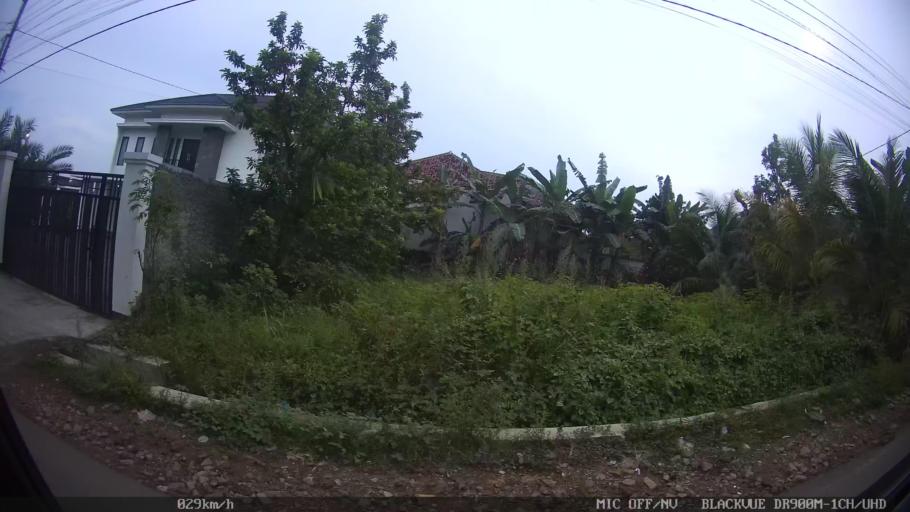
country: ID
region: Lampung
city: Kedaton
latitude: -5.4009
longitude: 105.2320
